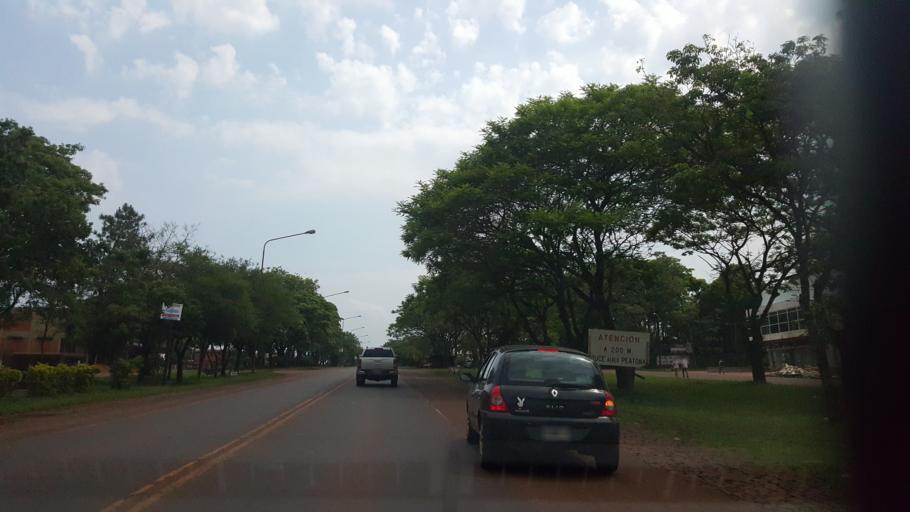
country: AR
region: Misiones
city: Jardin America
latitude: -27.0448
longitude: -55.2382
